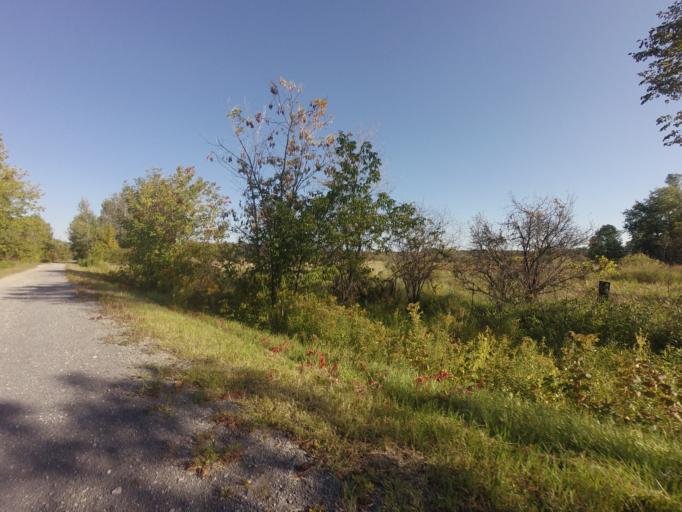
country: CA
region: Ontario
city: Hawkesbury
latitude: 45.5373
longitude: -74.6255
